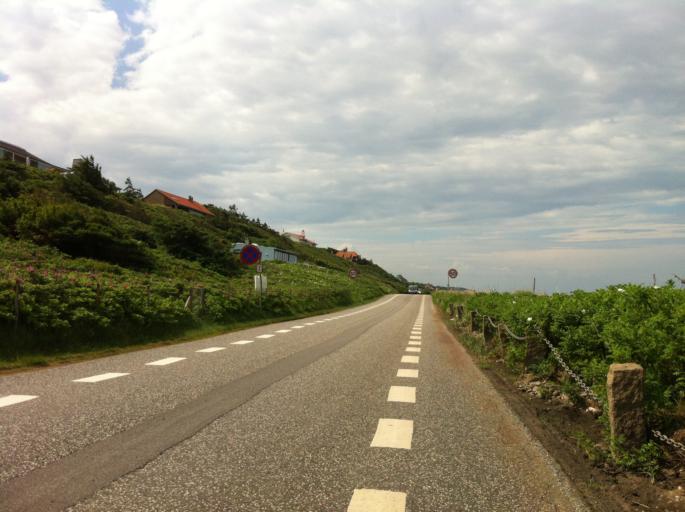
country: DK
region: Capital Region
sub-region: Gribskov Kommune
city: Helsinge
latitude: 56.1025
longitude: 12.1686
